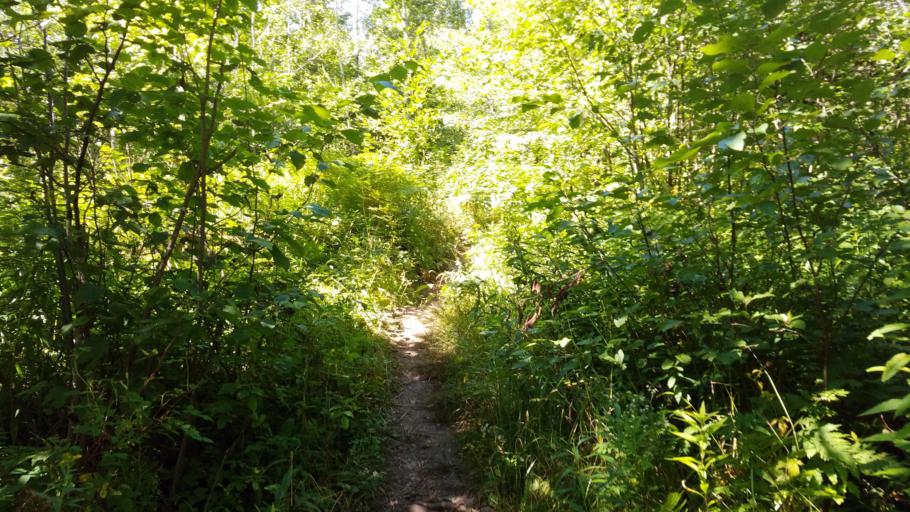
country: US
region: Michigan
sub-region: Ontonagon County
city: Ontonagon
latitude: 46.6506
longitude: -89.1563
